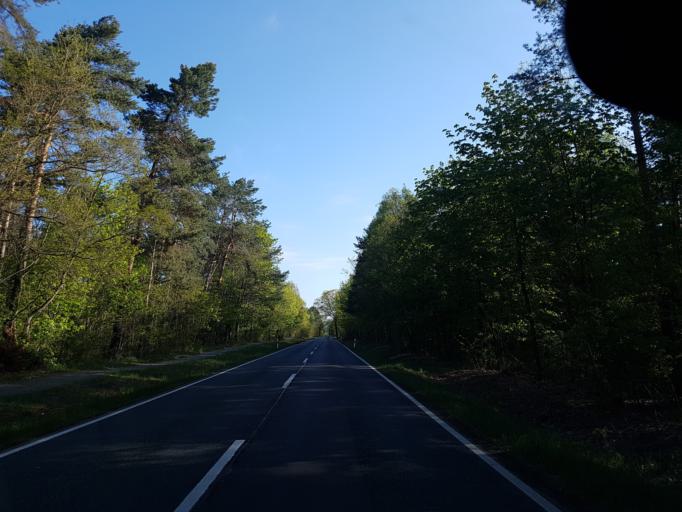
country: DE
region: Brandenburg
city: Grossraschen
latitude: 51.6031
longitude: 14.0173
